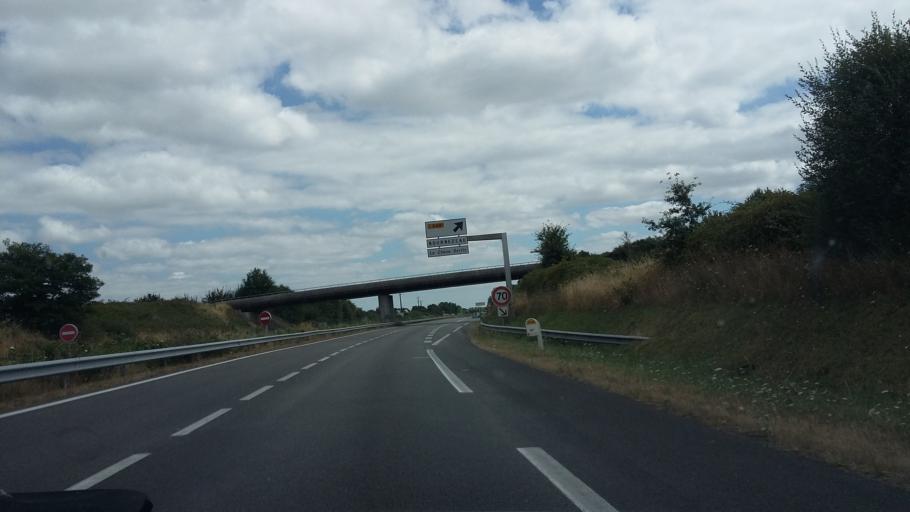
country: FR
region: Pays de la Loire
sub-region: Departement de la Vendee
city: Bournezeau
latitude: 46.6401
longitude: -1.1890
